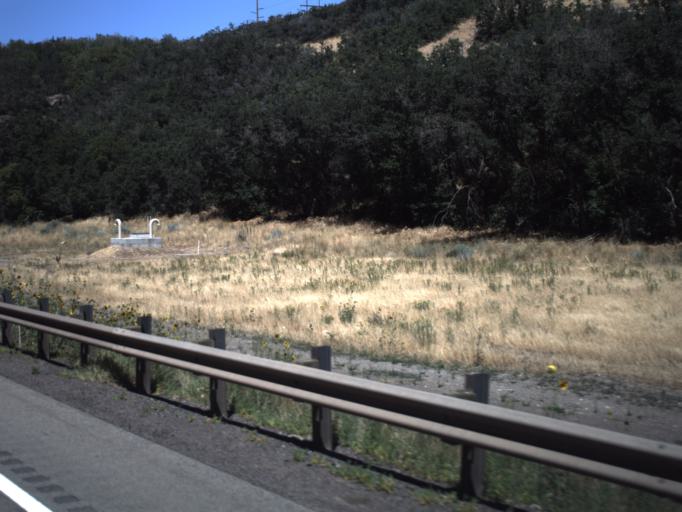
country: US
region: Utah
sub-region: Utah County
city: Mapleton
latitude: 40.0554
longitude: -111.5562
